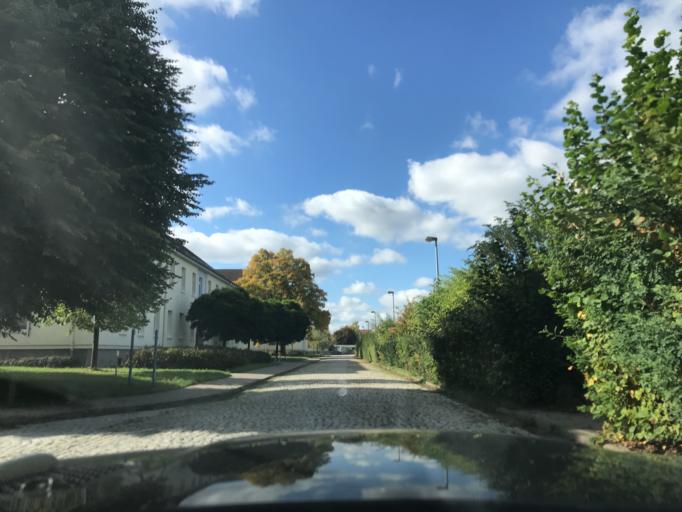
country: DE
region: Thuringia
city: Muehlhausen
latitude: 51.2158
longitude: 10.4816
